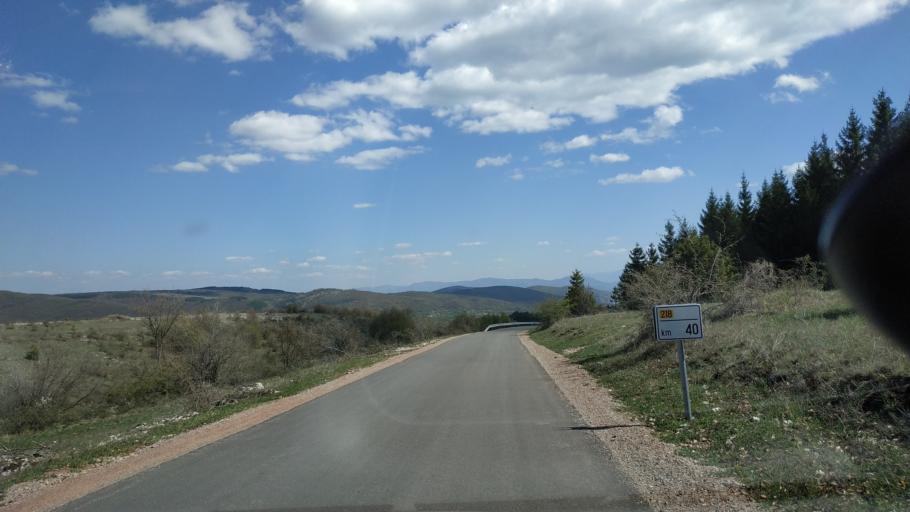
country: RS
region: Central Serbia
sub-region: Zajecarski Okrug
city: Soko Banja
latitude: 43.5811
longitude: 21.8943
